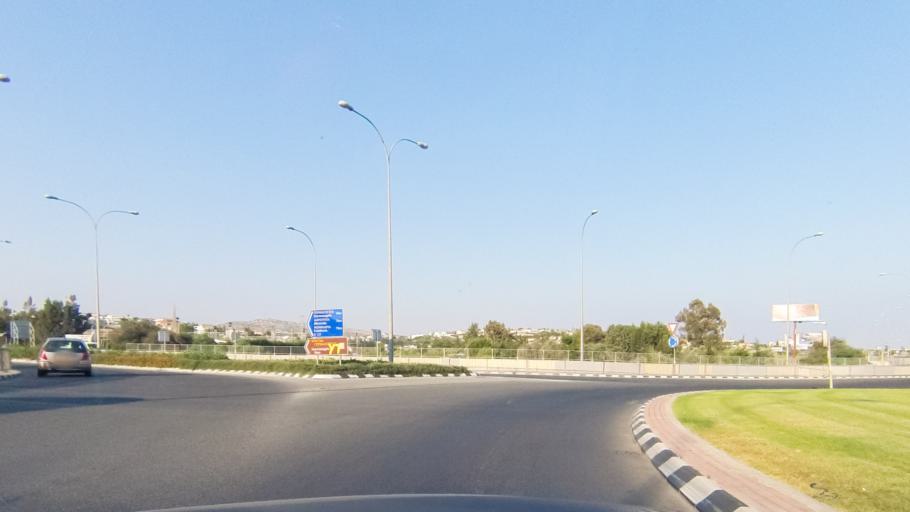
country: CY
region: Limassol
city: Mouttagiaka
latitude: 34.7085
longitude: 33.0865
